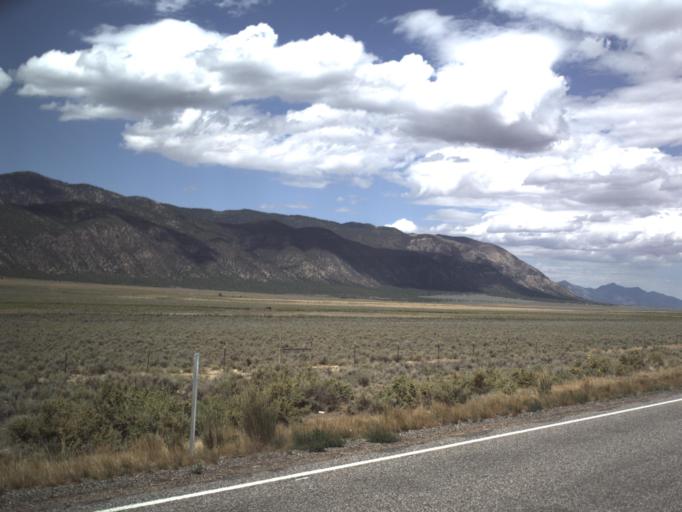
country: US
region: Utah
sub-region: Sevier County
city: Aurora
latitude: 39.0671
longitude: -112.0421
